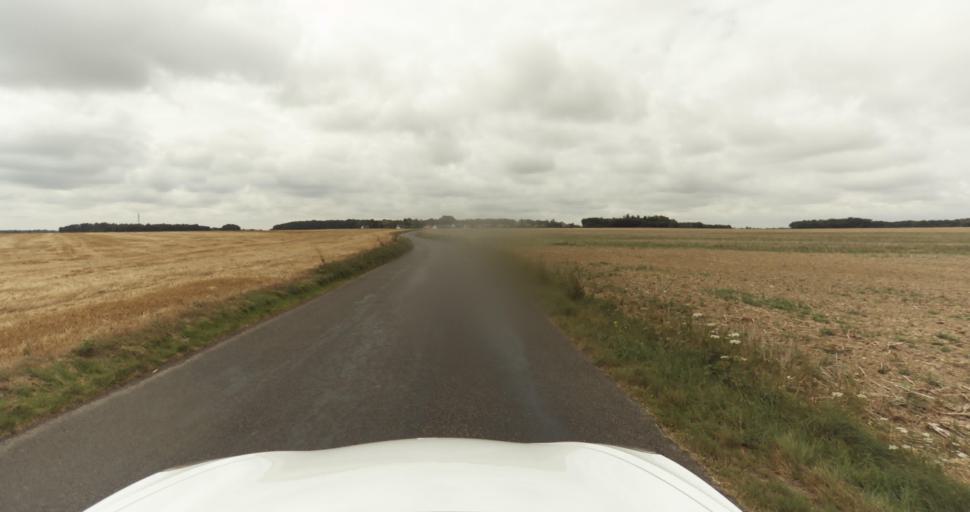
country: FR
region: Haute-Normandie
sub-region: Departement de l'Eure
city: Claville
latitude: 49.0324
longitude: 1.0538
